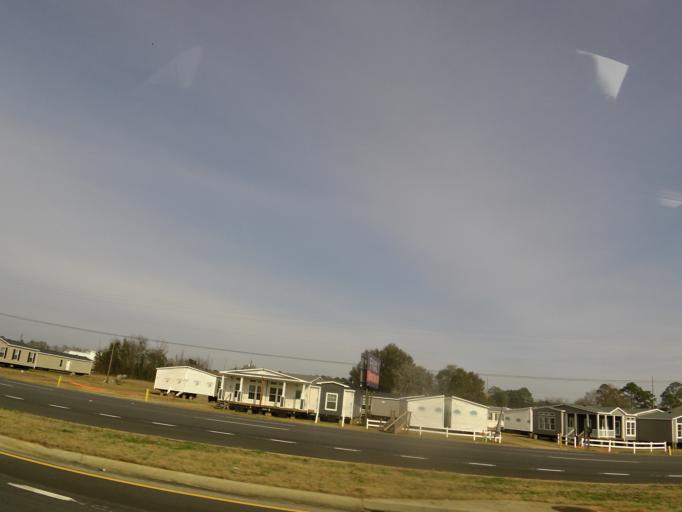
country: US
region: Alabama
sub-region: Dale County
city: Midland City
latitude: 31.2723
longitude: -85.4503
